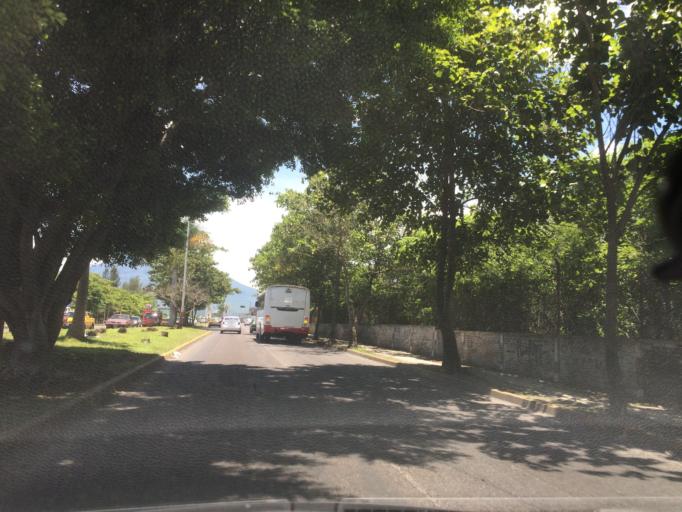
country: MX
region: Nayarit
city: Tepic
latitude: 21.4896
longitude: -104.8578
